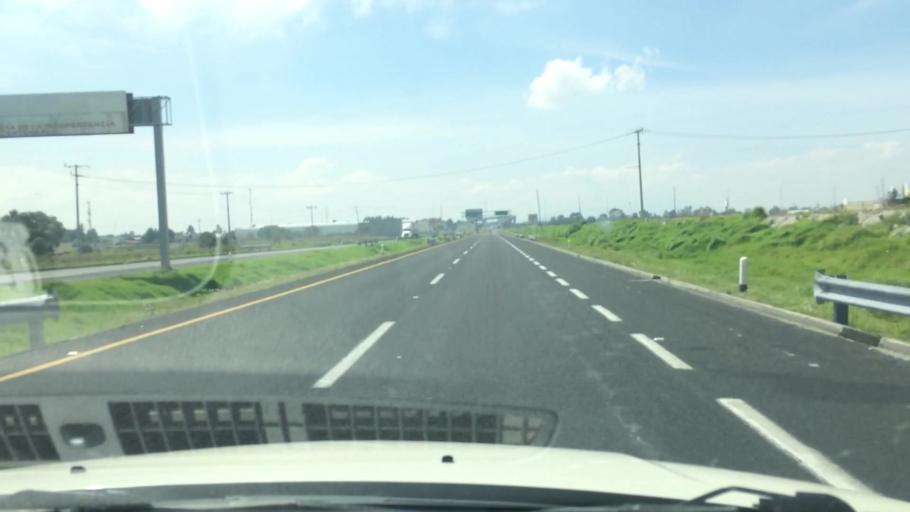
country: MX
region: Mexico
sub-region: Lerma
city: Colonia Isidro Fabela
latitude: 19.2950
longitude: -99.5214
